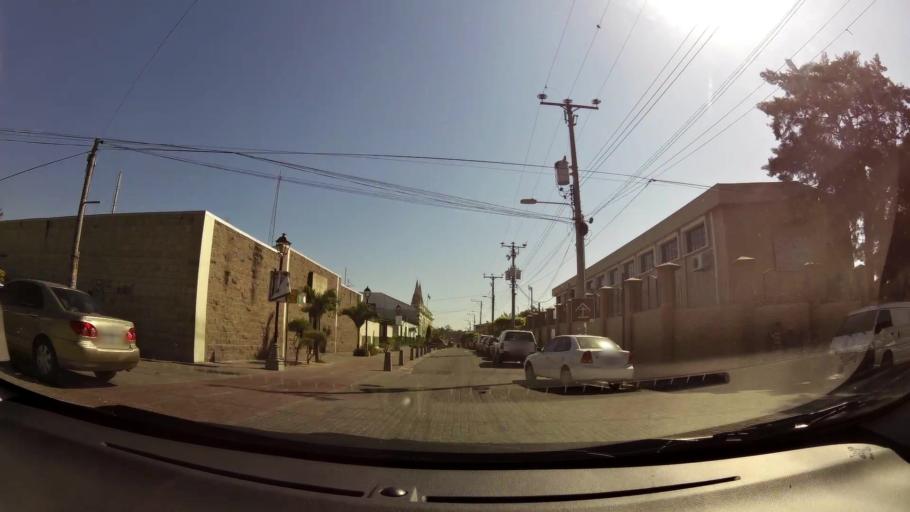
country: SV
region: La Libertad
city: Santa Tecla
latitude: 13.6755
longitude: -89.2902
